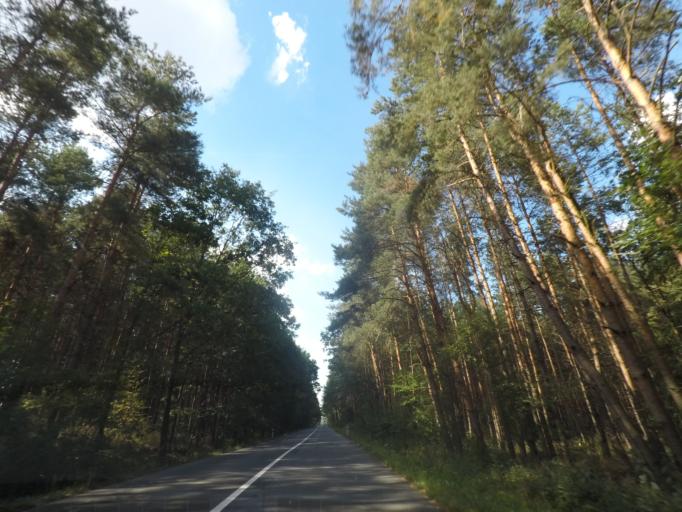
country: CZ
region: Kralovehradecky
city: Trebechovice pod Orebem
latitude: 50.2203
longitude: 15.9763
